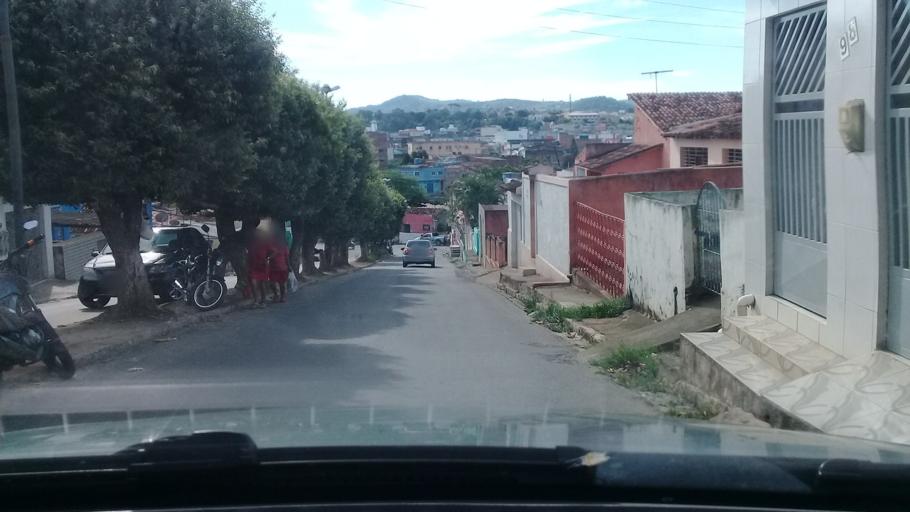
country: BR
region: Pernambuco
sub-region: Vitoria De Santo Antao
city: Vitoria de Santo Antao
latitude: -8.1235
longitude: -35.2926
